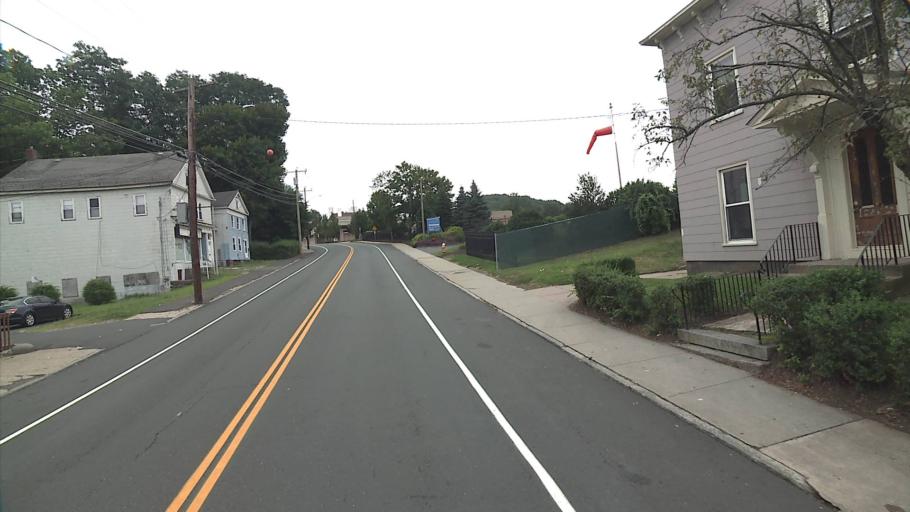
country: US
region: Connecticut
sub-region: Tolland County
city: Rockville
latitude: 41.8671
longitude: -72.4532
